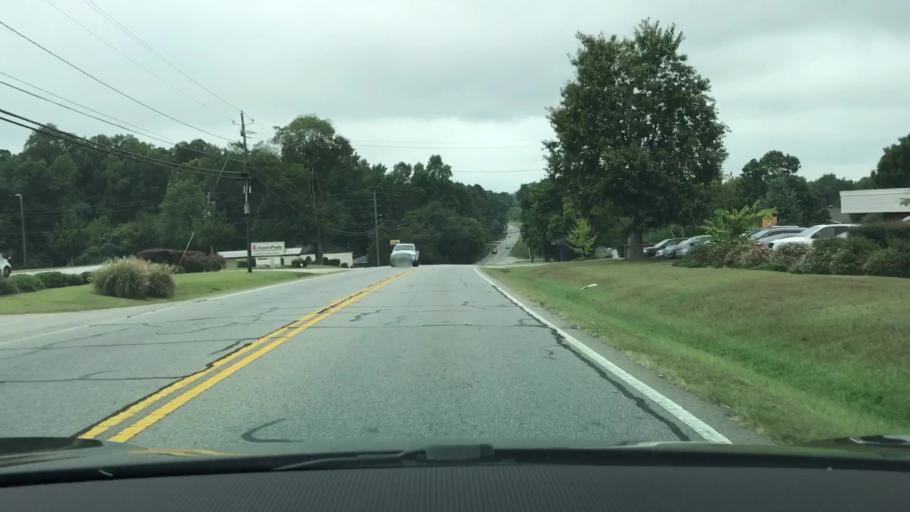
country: US
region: Georgia
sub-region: Oconee County
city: Watkinsville
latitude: 33.8663
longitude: -83.4133
